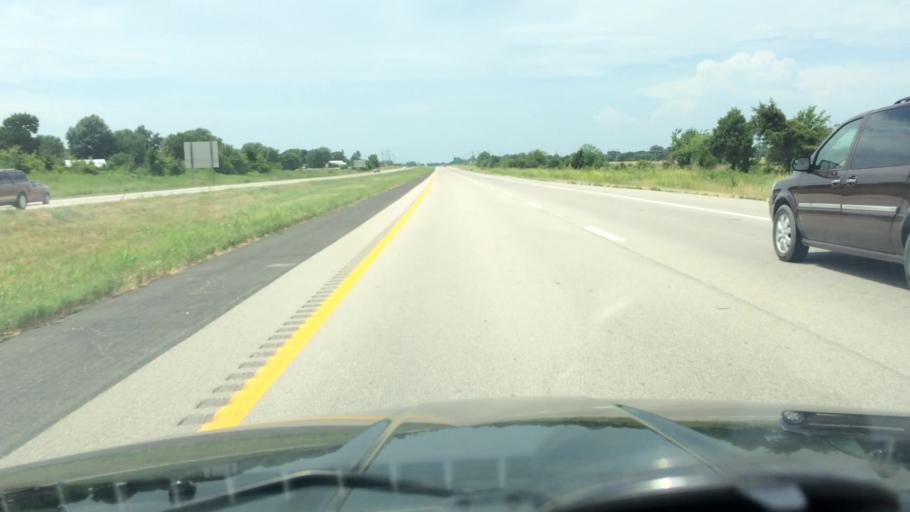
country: US
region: Missouri
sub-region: Polk County
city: Bolivar
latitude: 37.5793
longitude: -93.4043
